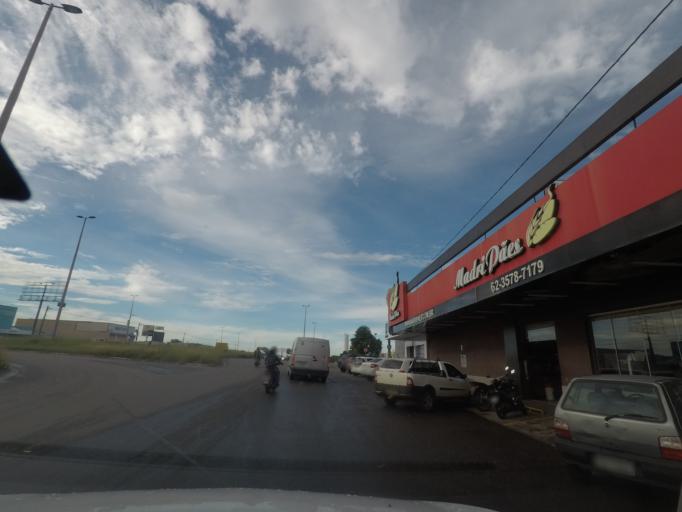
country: BR
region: Goias
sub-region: Aparecida De Goiania
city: Aparecida de Goiania
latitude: -16.7684
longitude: -49.3511
